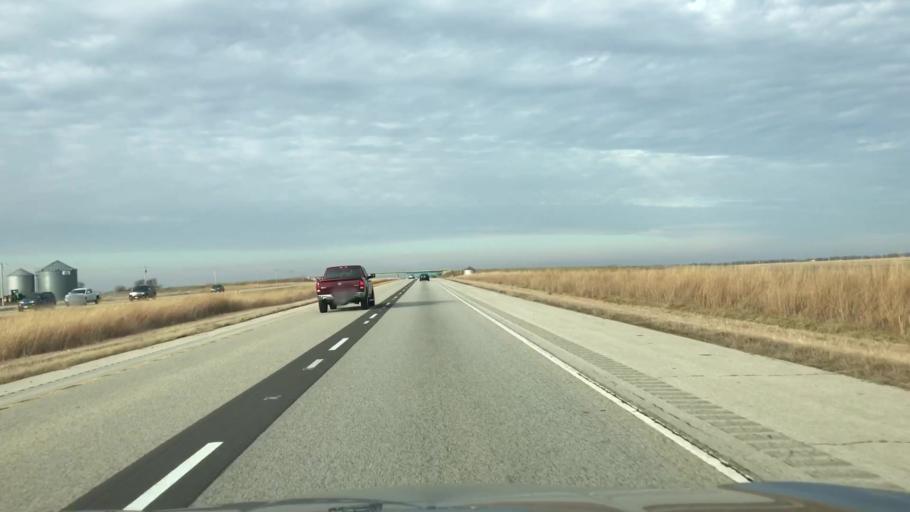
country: US
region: Illinois
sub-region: Sangamon County
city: Divernon
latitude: 39.4742
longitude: -89.6445
